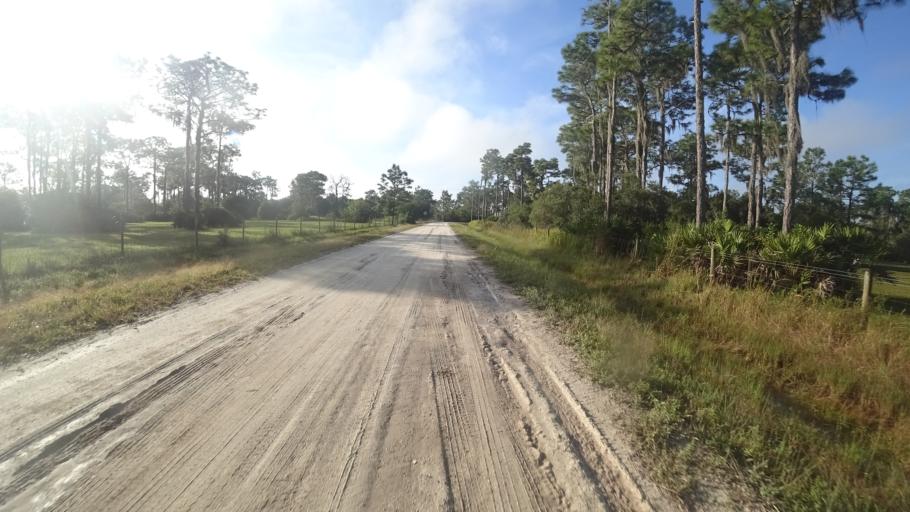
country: US
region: Florida
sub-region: Sarasota County
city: Fruitville
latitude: 27.4062
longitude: -82.2916
